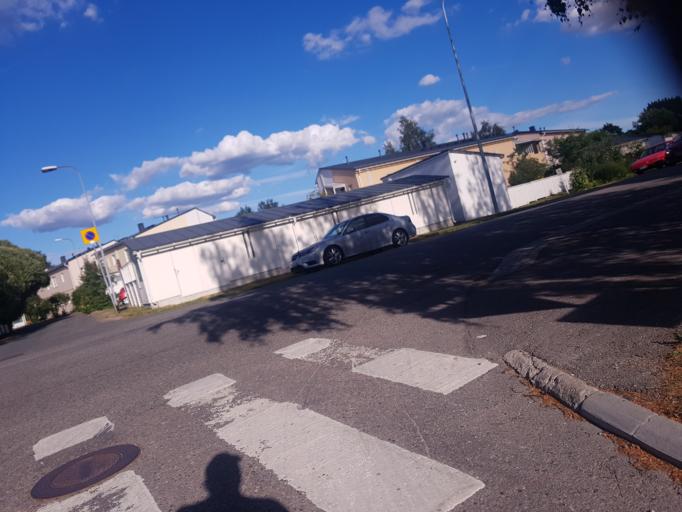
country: FI
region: Uusimaa
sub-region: Helsinki
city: Vantaa
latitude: 60.2667
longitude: 24.9802
